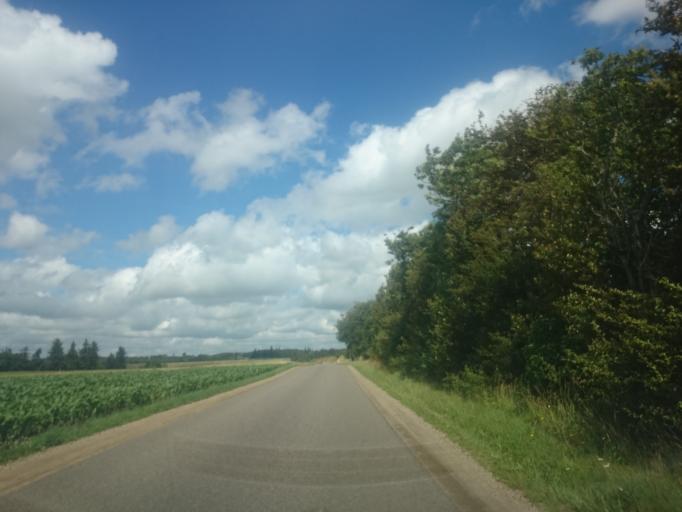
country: DK
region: South Denmark
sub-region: Billund Kommune
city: Billund
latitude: 55.7329
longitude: 9.2032
